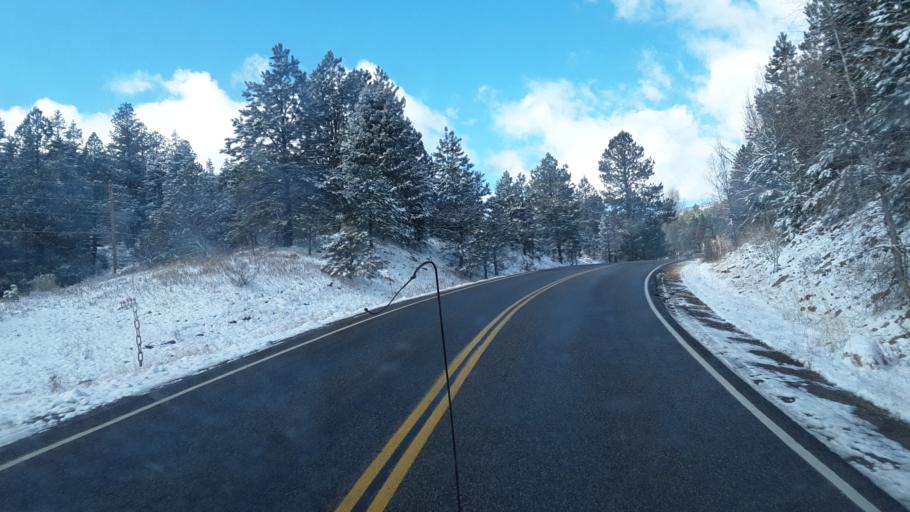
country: US
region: Colorado
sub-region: La Plata County
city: Bayfield
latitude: 37.3539
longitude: -107.6549
